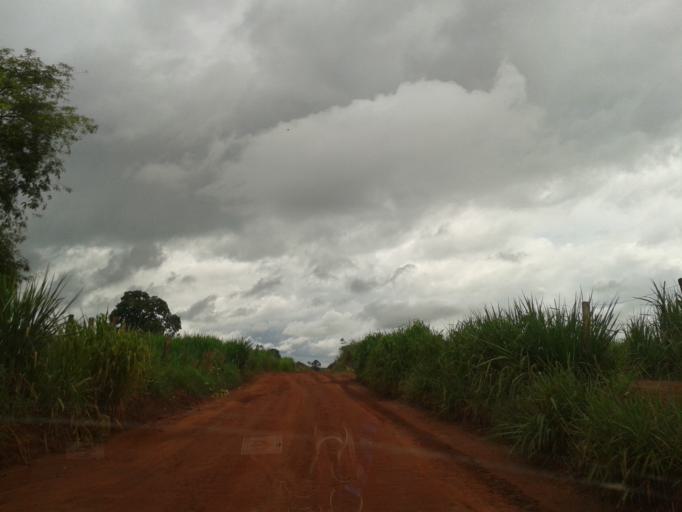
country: BR
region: Minas Gerais
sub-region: Santa Vitoria
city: Santa Vitoria
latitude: -18.6840
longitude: -49.9389
